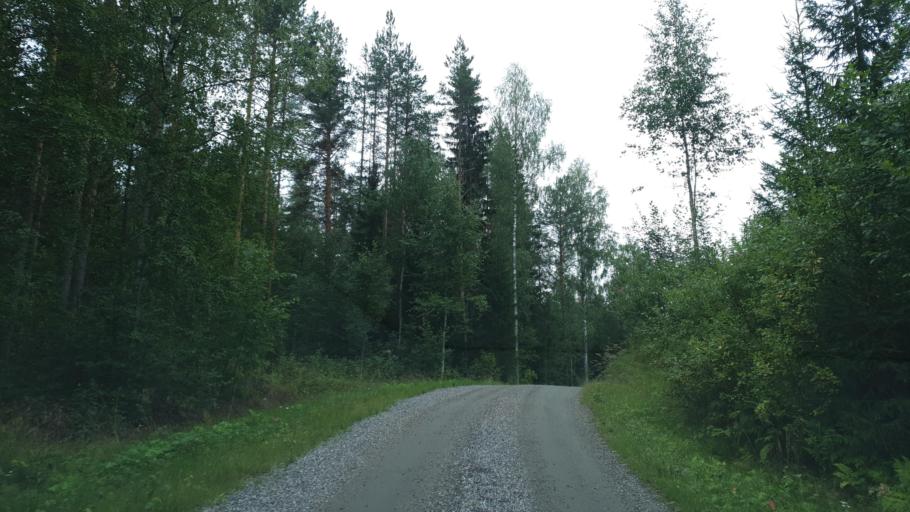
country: FI
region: Northern Savo
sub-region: Kuopio
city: Nilsiae
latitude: 63.2425
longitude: 28.2554
